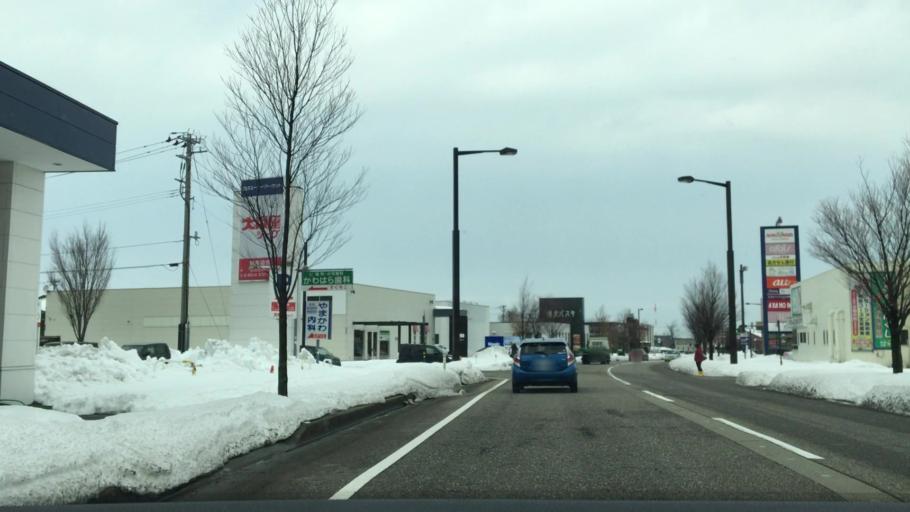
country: JP
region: Ishikawa
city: Nonoichi
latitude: 36.5169
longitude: 136.6089
